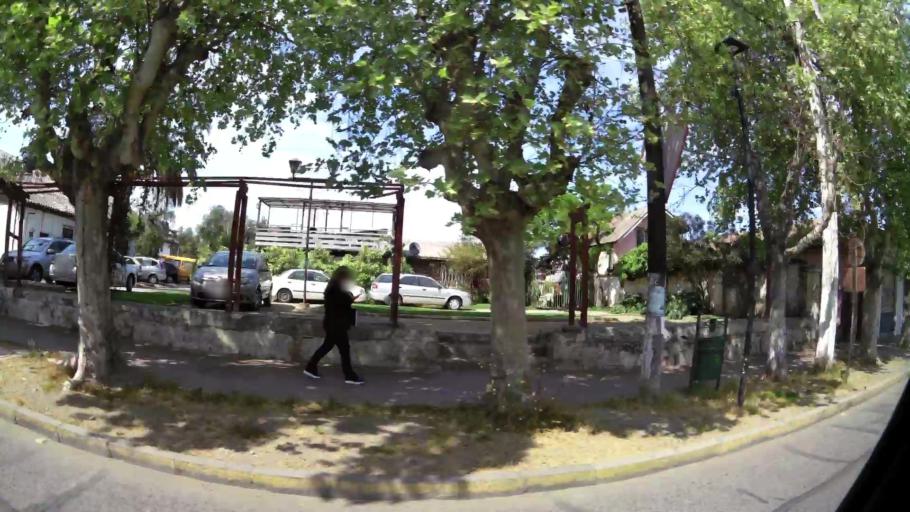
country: CL
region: Santiago Metropolitan
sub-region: Provincia de Talagante
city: Talagante
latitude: -33.6618
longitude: -70.9231
